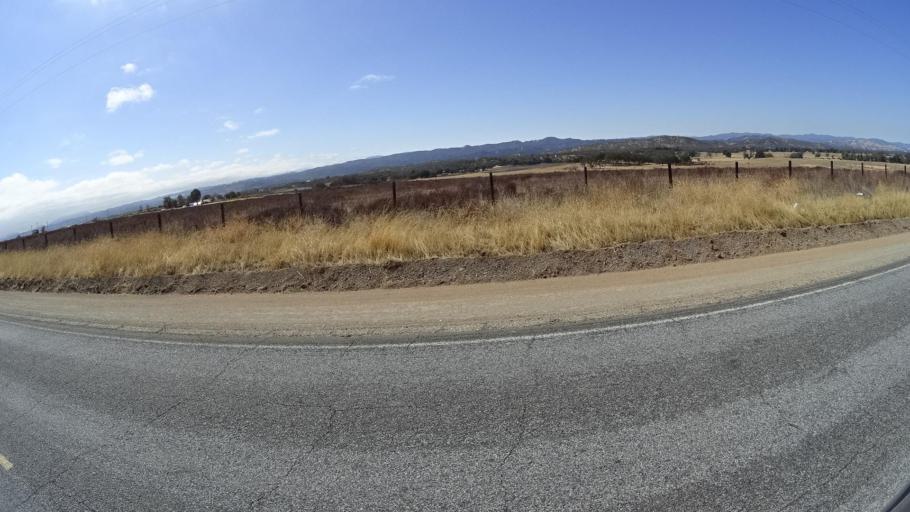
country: US
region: California
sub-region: San Luis Obispo County
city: Lake Nacimiento
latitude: 35.9272
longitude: -121.0458
